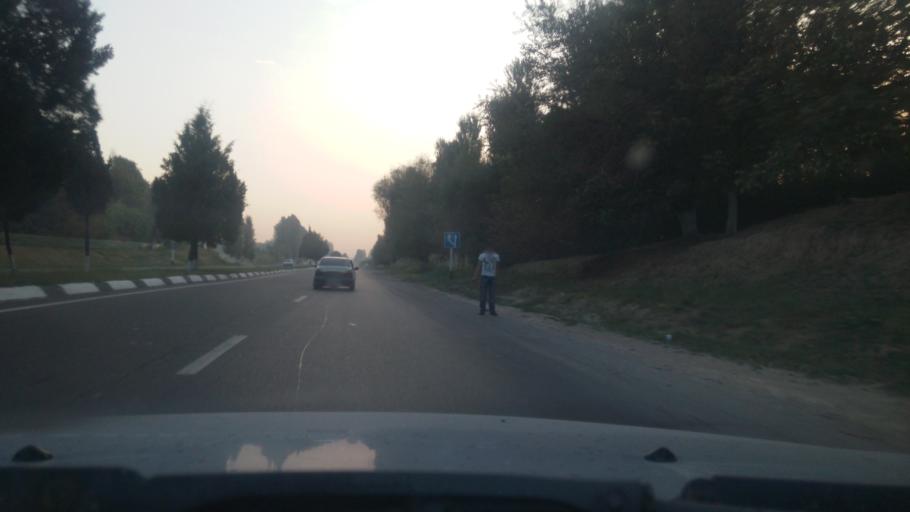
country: UZ
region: Toshkent
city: Amir Timur
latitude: 41.0690
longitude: 68.9218
